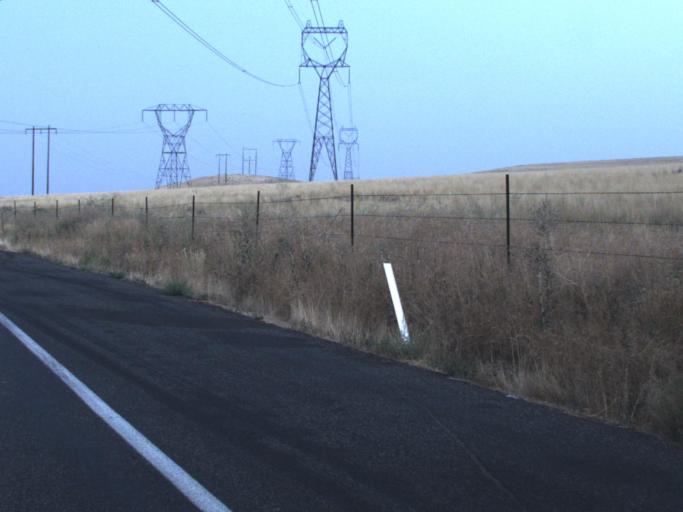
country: US
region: Washington
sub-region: Yakima County
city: Sunnyside
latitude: 46.4725
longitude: -119.9315
